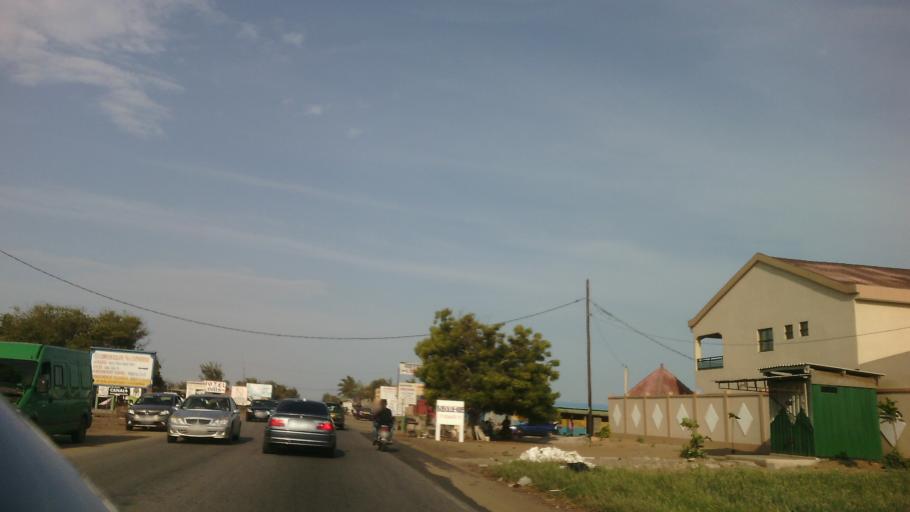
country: TG
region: Maritime
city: Lome
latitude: 6.1779
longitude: 1.3748
